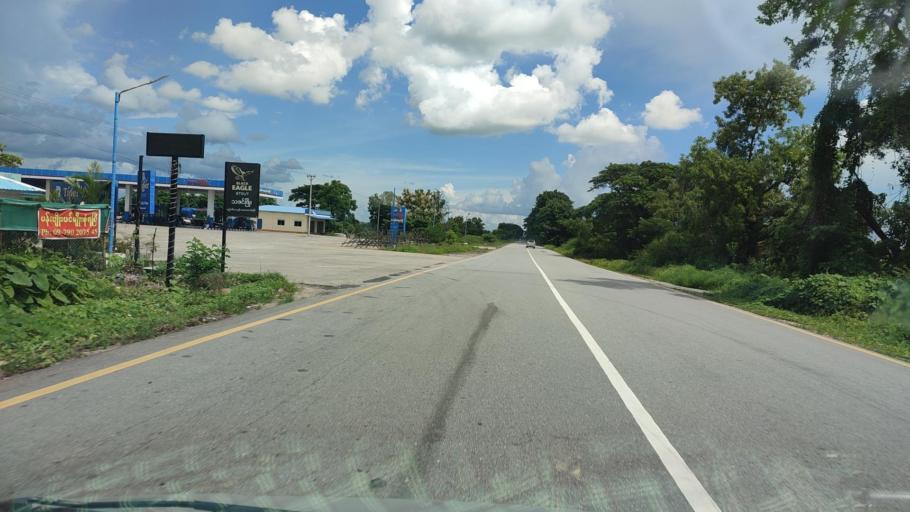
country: MM
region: Bago
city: Nyaunglebin
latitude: 18.0159
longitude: 96.6935
